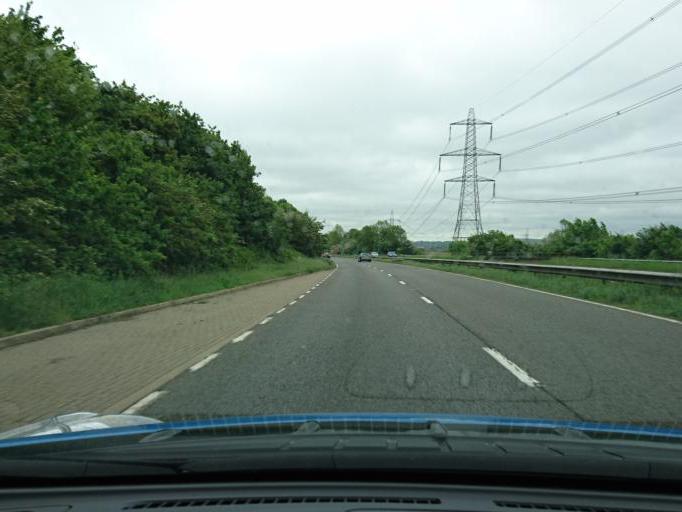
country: GB
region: England
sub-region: Oxfordshire
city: Boars Hill
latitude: 51.7543
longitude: -1.3062
